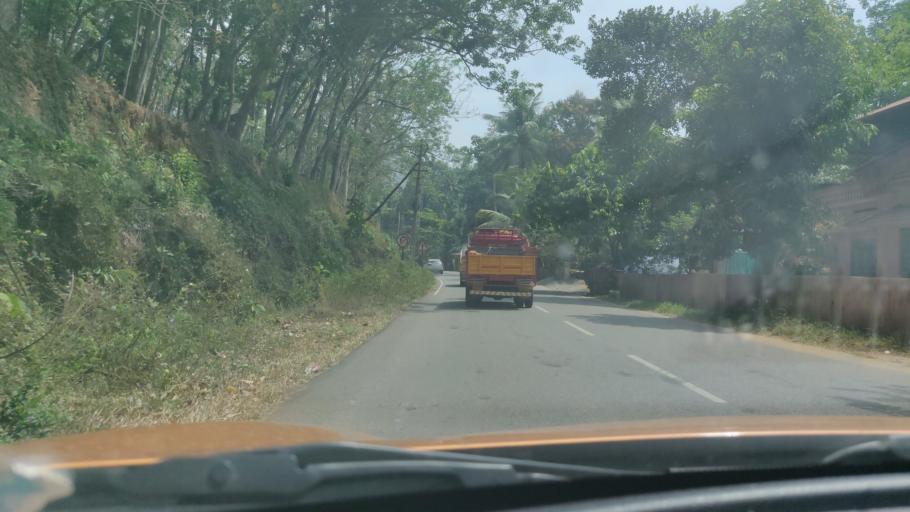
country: IN
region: Kerala
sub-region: Ernakulam
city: Muvattupuzha
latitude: 9.8853
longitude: 76.6523
